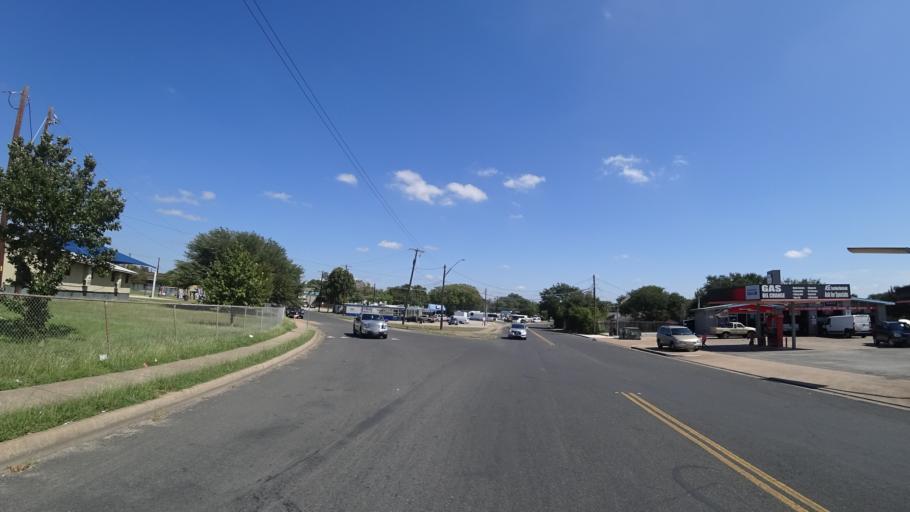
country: US
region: Texas
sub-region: Travis County
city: Austin
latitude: 30.3138
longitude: -97.6908
